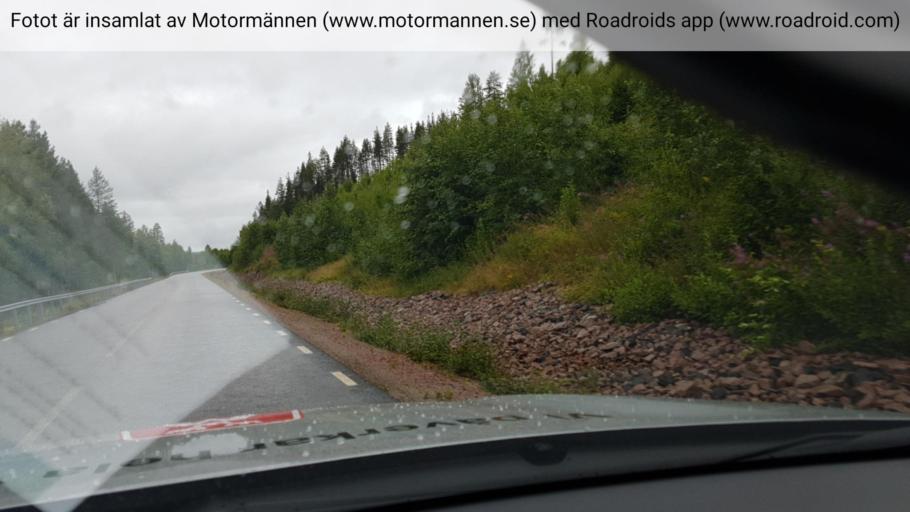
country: SE
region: Norrbotten
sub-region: Gallivare Kommun
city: Gaellivare
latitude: 66.6263
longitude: 20.4176
